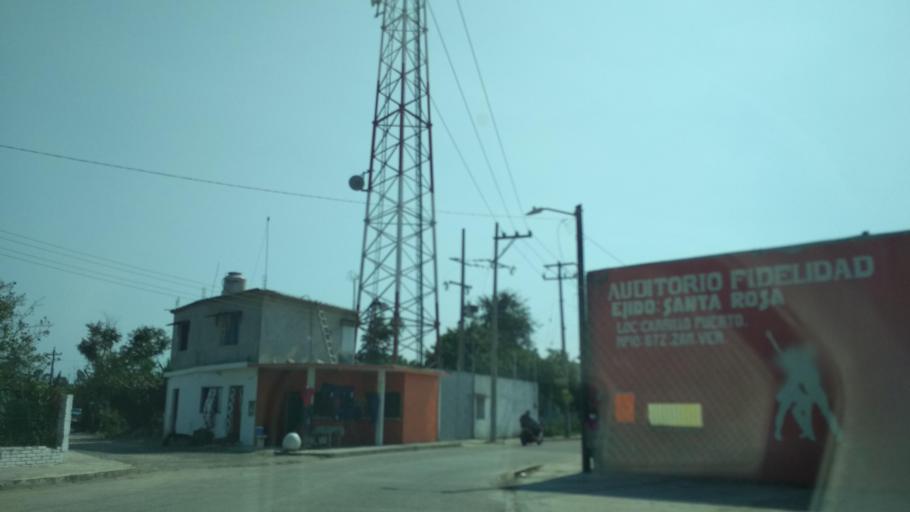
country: MX
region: Veracruz
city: Gutierrez Zamora
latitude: 20.4199
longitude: -97.1878
